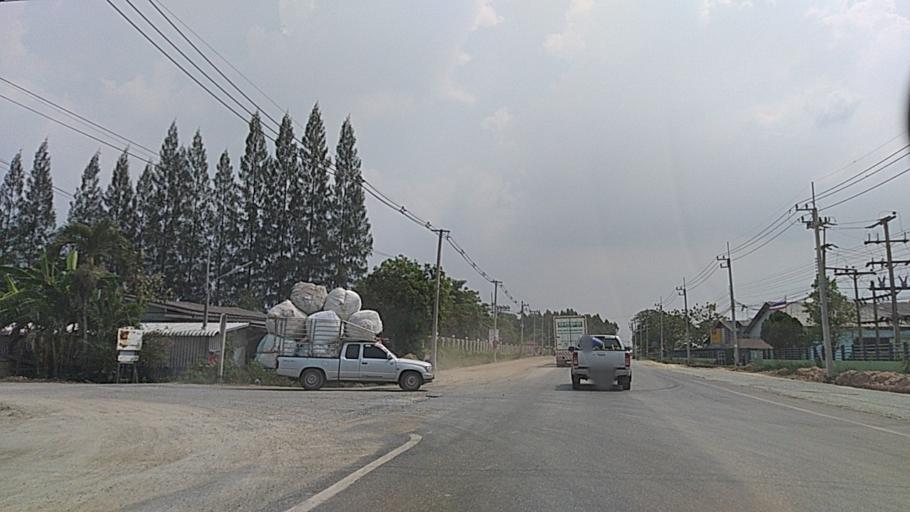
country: TH
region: Chon Buri
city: Phanat Nikhom
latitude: 13.3621
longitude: 101.1966
